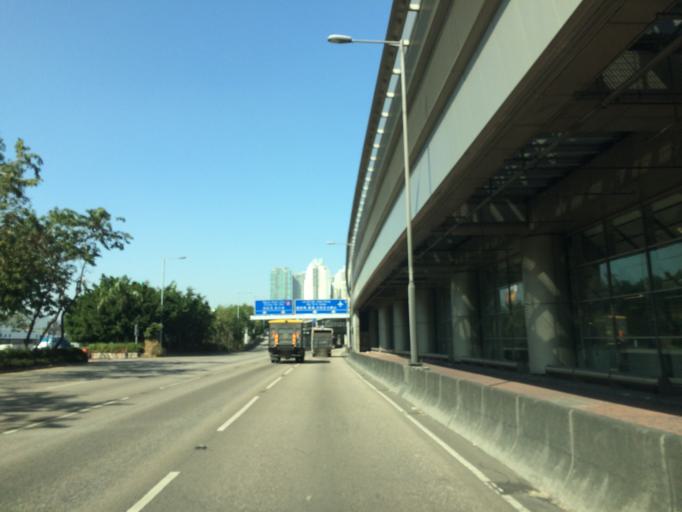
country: HK
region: Sham Shui Po
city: Sham Shui Po
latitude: 22.3260
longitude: 114.1533
